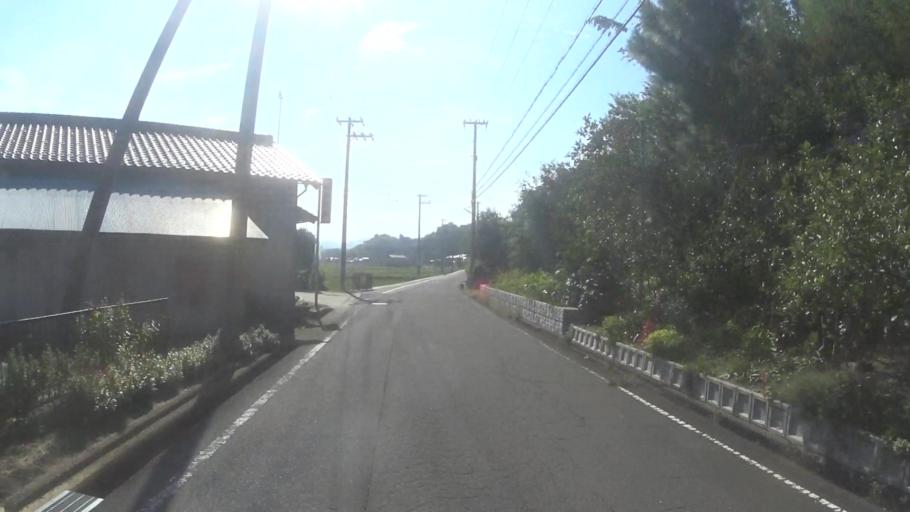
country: JP
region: Kyoto
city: Miyazu
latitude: 35.6802
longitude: 135.0883
